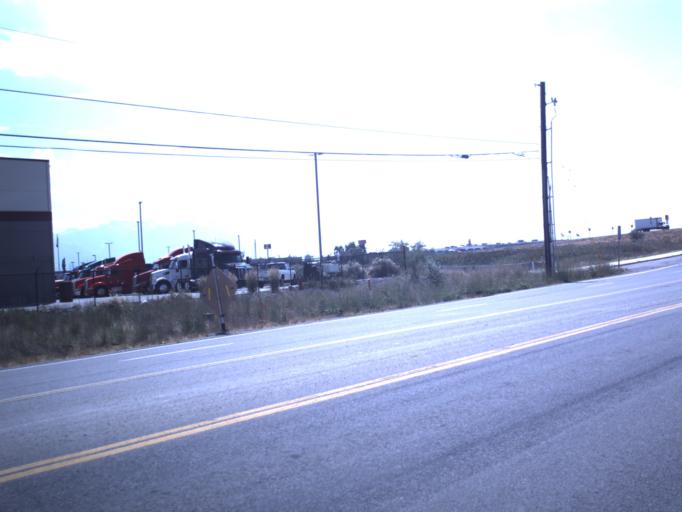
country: US
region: Utah
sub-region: Salt Lake County
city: West Valley City
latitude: 40.7292
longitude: -112.0250
